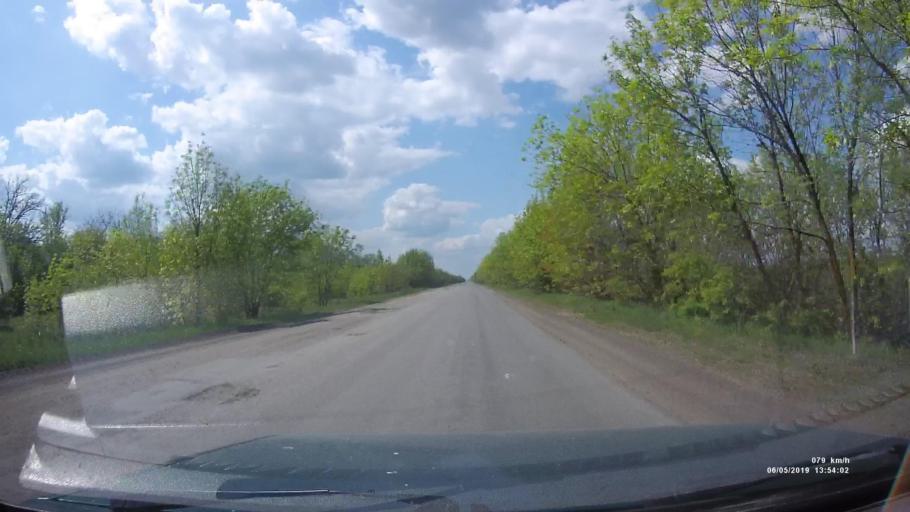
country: RU
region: Rostov
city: Melikhovskaya
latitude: 47.6721
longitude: 40.4531
